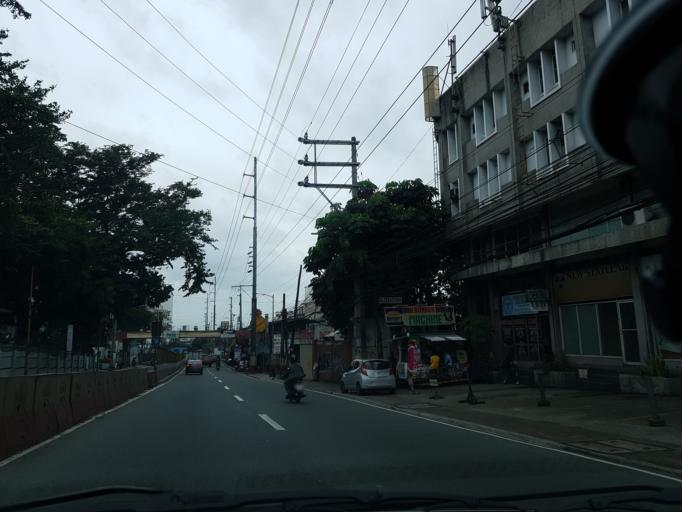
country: PH
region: Metro Manila
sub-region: Pasig
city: Pasig City
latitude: 14.5648
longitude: 121.0656
